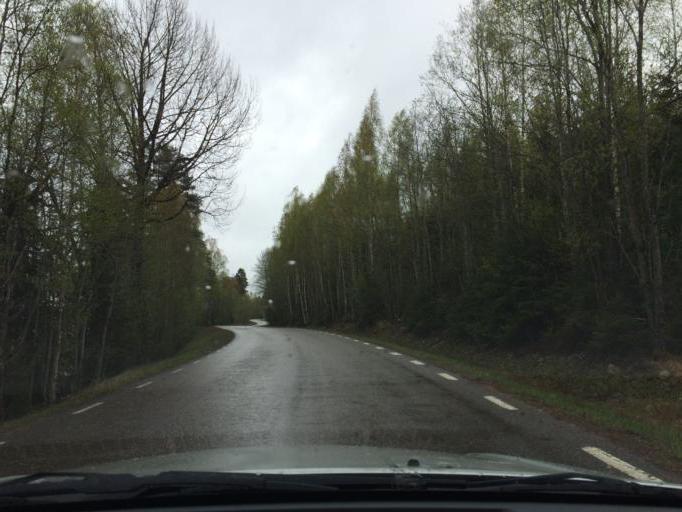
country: SE
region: Dalarna
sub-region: Ludvika Kommun
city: Grangesberg
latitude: 60.0603
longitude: 14.8818
